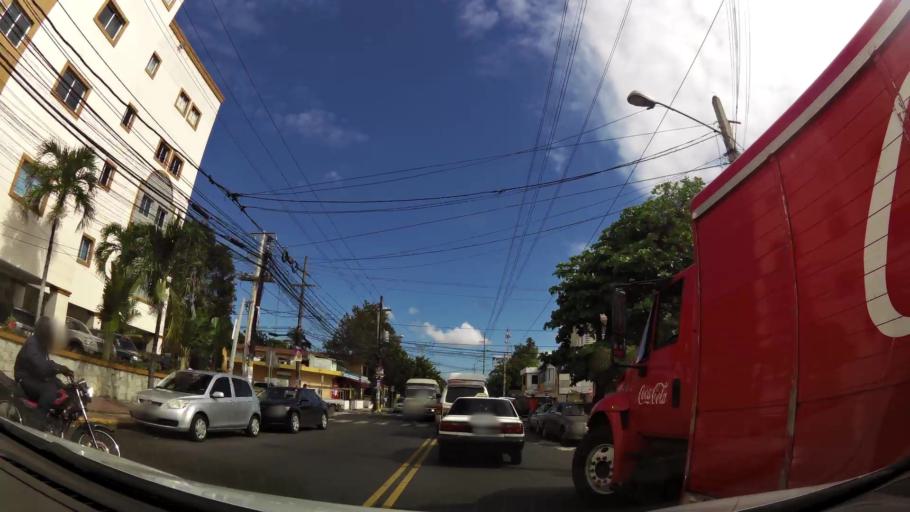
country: DO
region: Santo Domingo
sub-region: Santo Domingo
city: Santo Domingo Este
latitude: 18.4879
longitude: -69.8655
